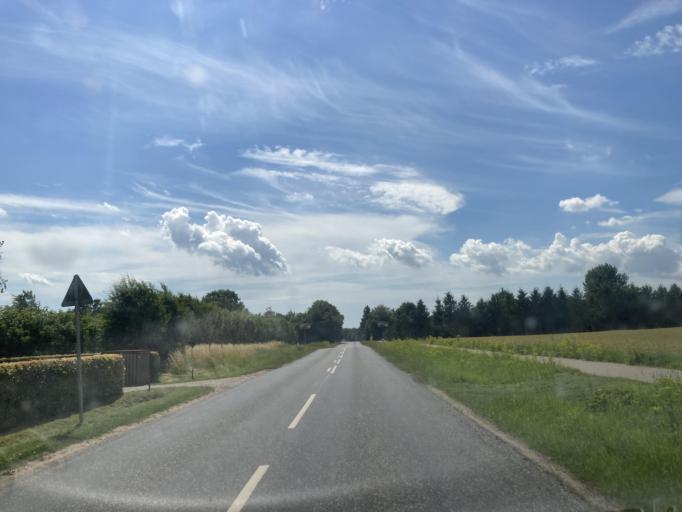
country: DK
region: Zealand
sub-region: Faxe Kommune
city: Haslev
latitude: 55.3722
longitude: 11.9629
